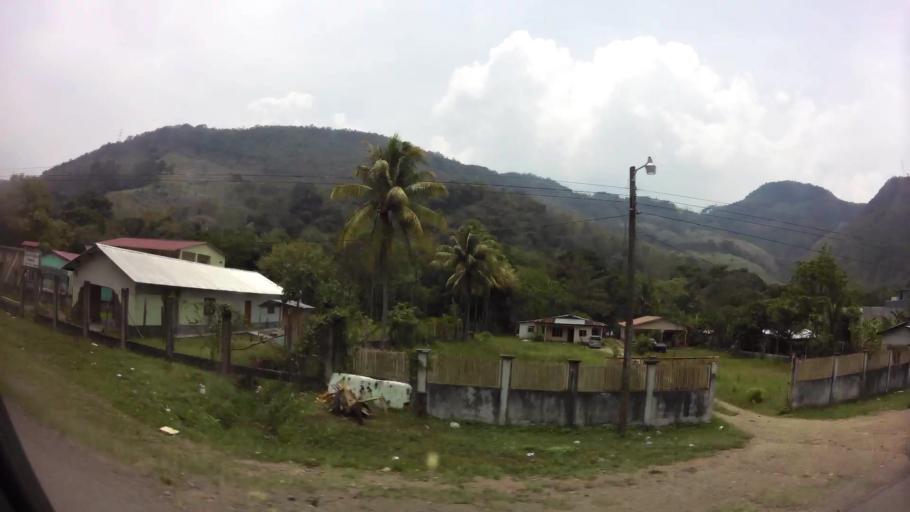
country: HN
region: Comayagua
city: Taulabe
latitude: 14.7342
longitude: -87.9645
